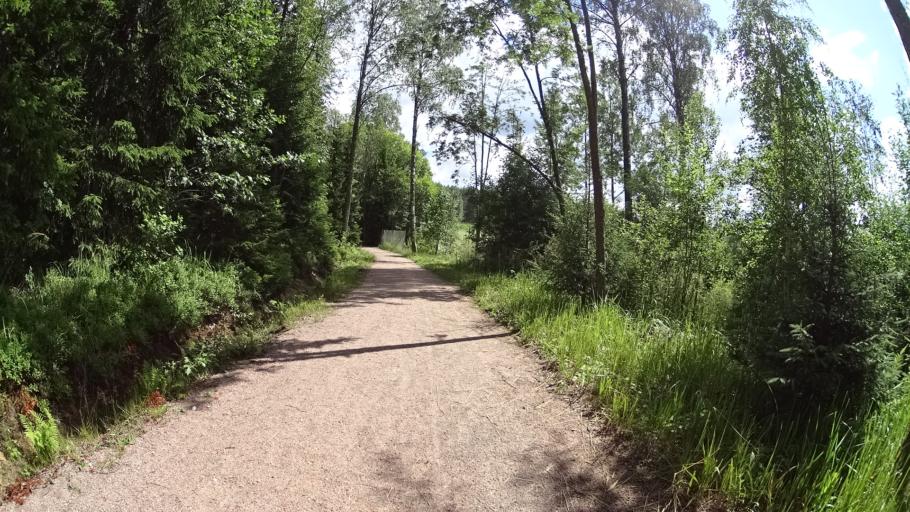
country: FI
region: Uusimaa
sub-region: Helsinki
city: Espoo
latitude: 60.3208
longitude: 24.6721
